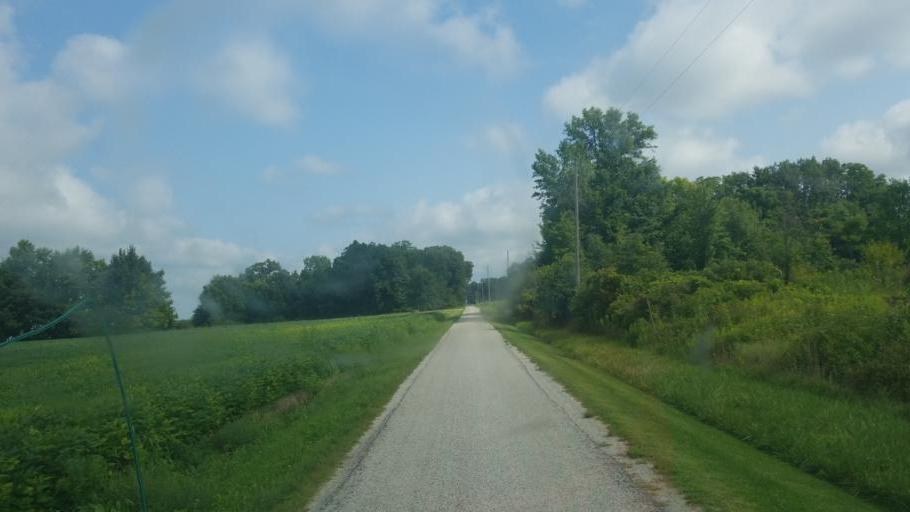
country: US
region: Ohio
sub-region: Marion County
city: Marion
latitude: 40.5709
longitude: -83.0053
